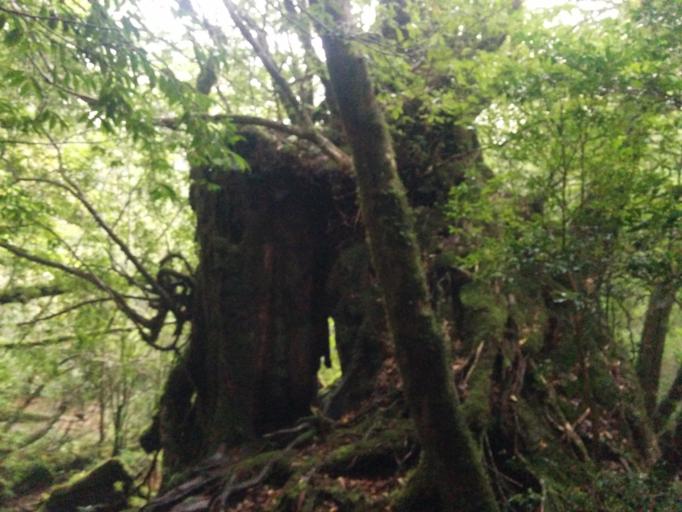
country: JP
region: Kagoshima
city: Nishinoomote
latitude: 30.3674
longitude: 130.5692
